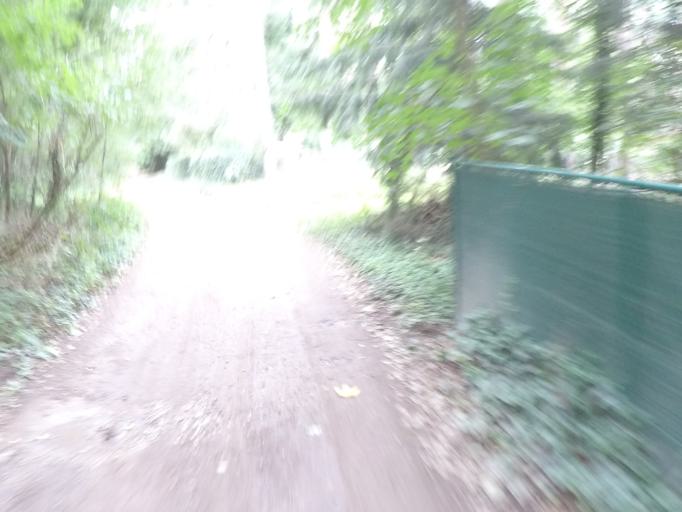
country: BE
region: Flanders
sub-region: Provincie Antwerpen
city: Grobbendonk
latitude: 51.2051
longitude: 4.7412
